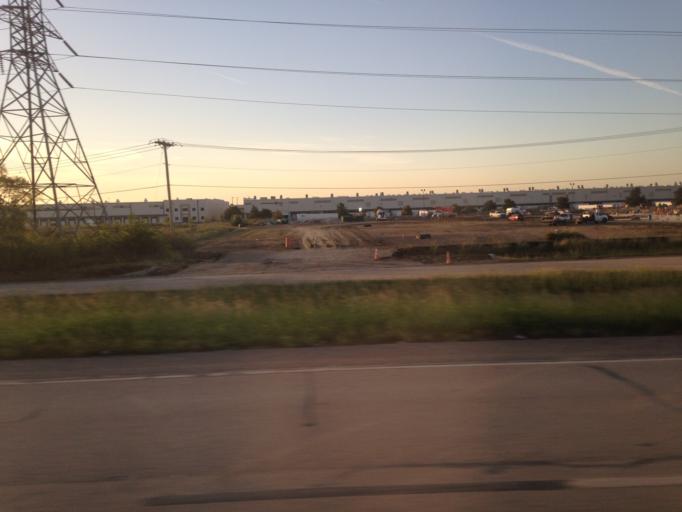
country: US
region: Texas
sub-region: Tarrant County
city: Blue Mound
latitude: 32.8411
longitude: -97.3510
